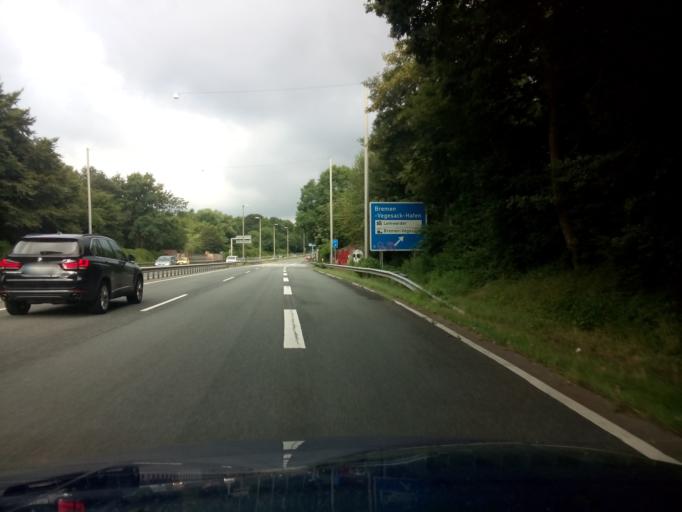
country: DE
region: Lower Saxony
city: Lemwerder
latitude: 53.1751
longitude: 8.6423
